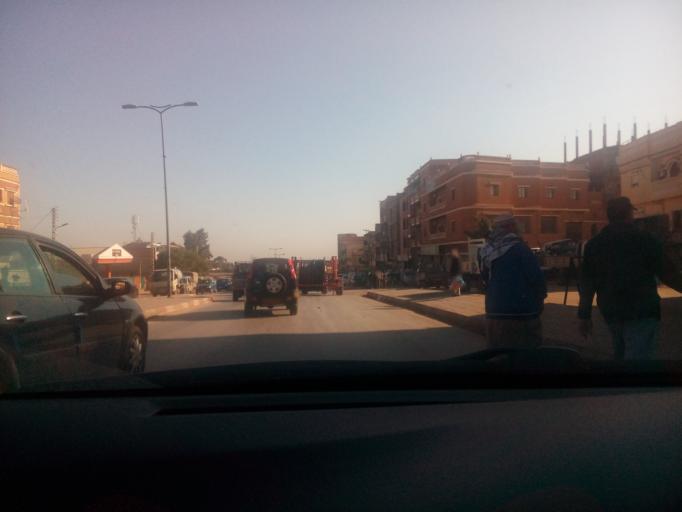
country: DZ
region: Oran
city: Oran
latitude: 35.6612
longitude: -0.6897
